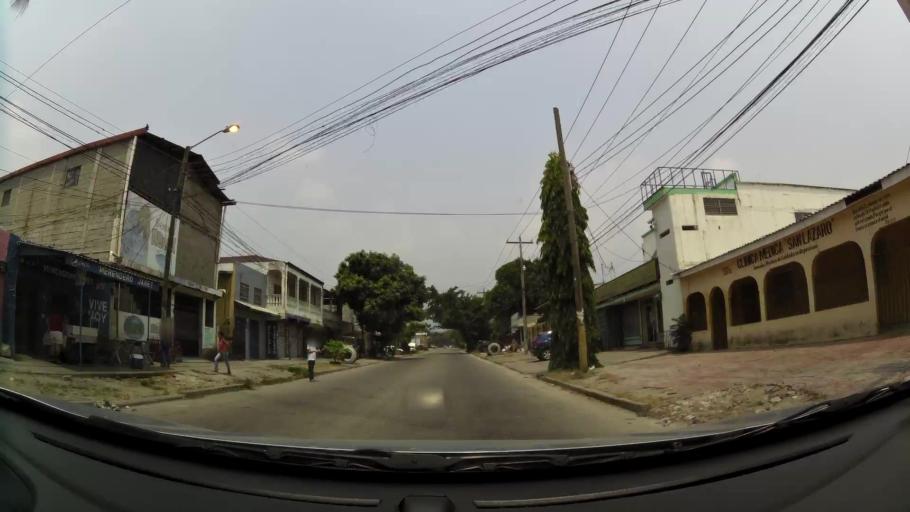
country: HN
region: Cortes
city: San Pedro Sula
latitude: 15.4854
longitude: -88.0117
